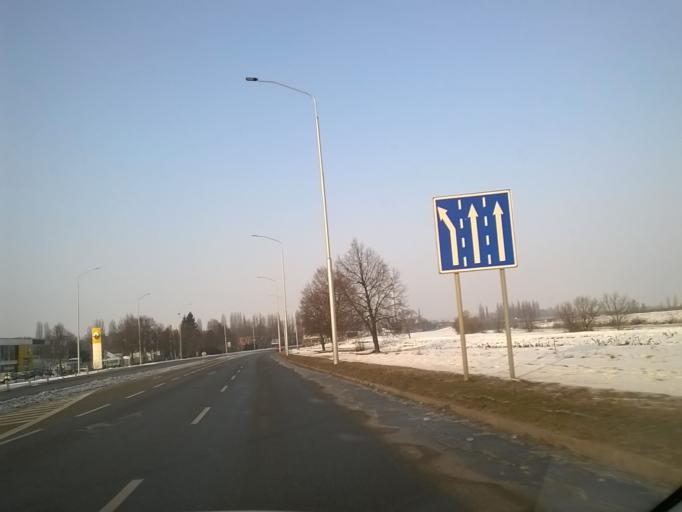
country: SK
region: Nitriansky
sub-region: Okres Nitra
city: Nitra
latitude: 48.3179
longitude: 18.0560
